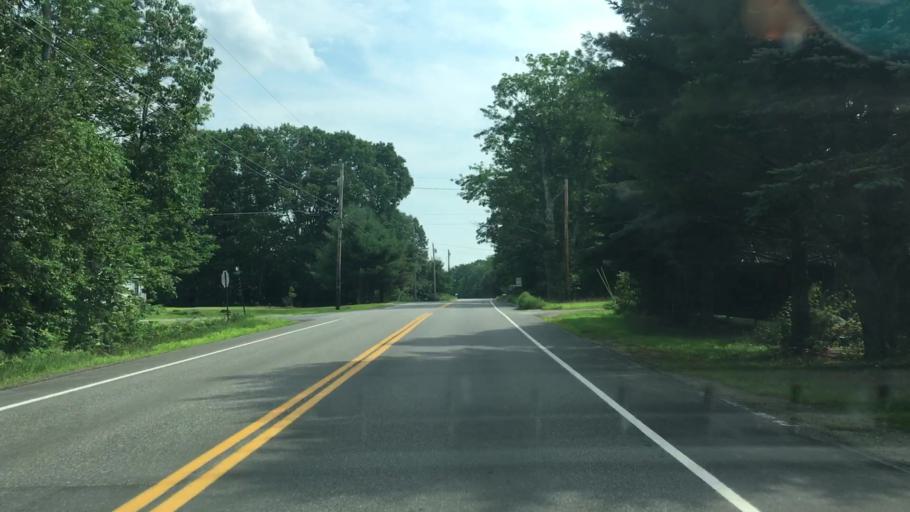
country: US
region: Maine
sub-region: Kennebec County
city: Windsor
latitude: 44.3391
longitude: -69.5820
